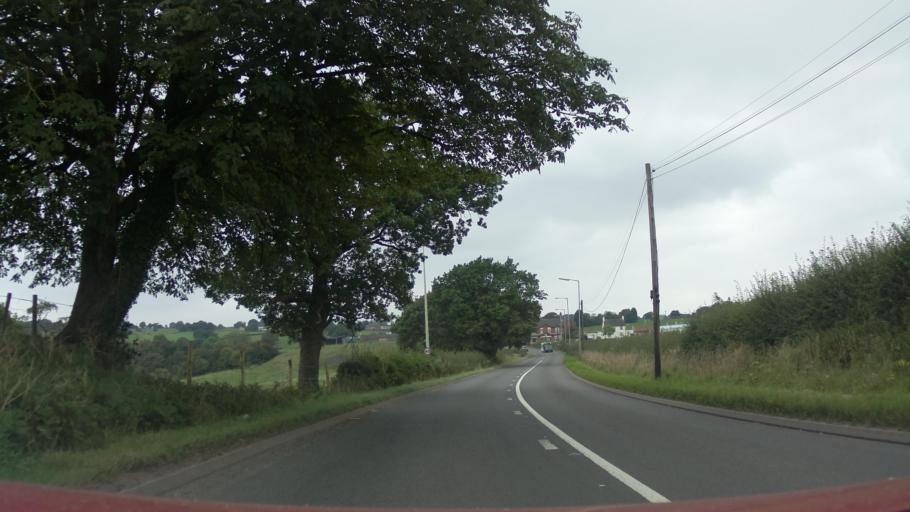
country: GB
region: England
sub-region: Staffordshire
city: Cheddleton
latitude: 53.0189
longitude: -2.0315
